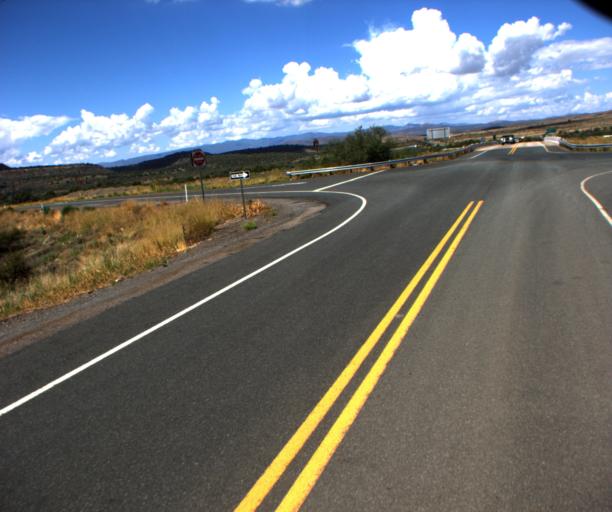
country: US
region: Arizona
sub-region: Yavapai County
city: Camp Verde
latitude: 34.5141
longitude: -111.9909
